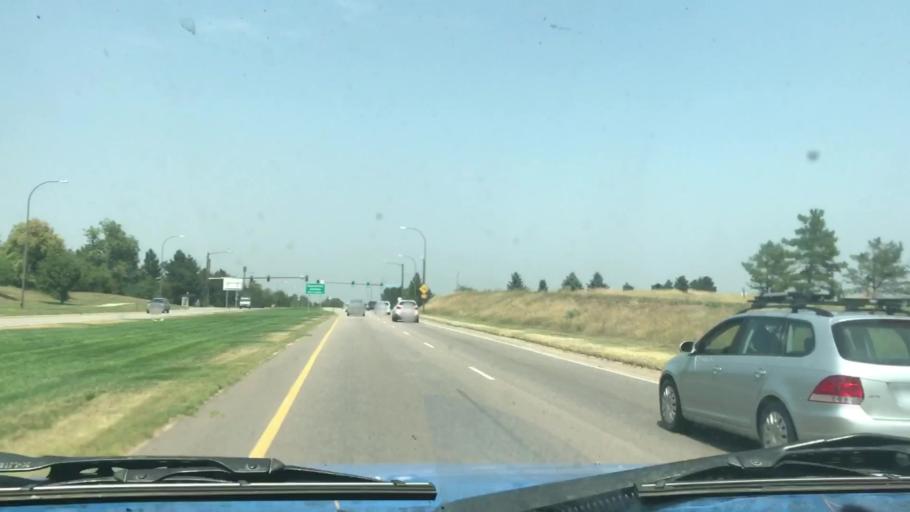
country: US
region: Colorado
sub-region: Jefferson County
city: Lakewood
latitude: 39.7018
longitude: -105.1096
